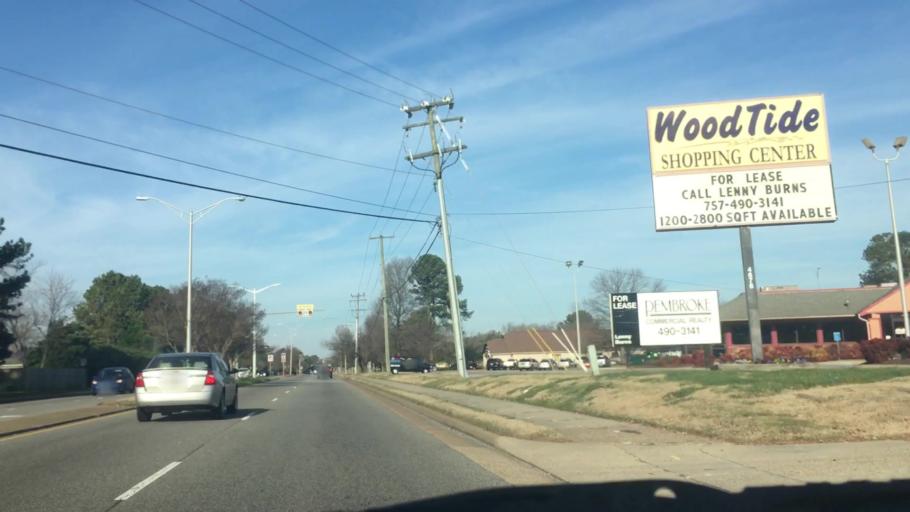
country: US
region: Virginia
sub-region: City of Chesapeake
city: Chesapeake
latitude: 36.8114
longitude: -76.1392
